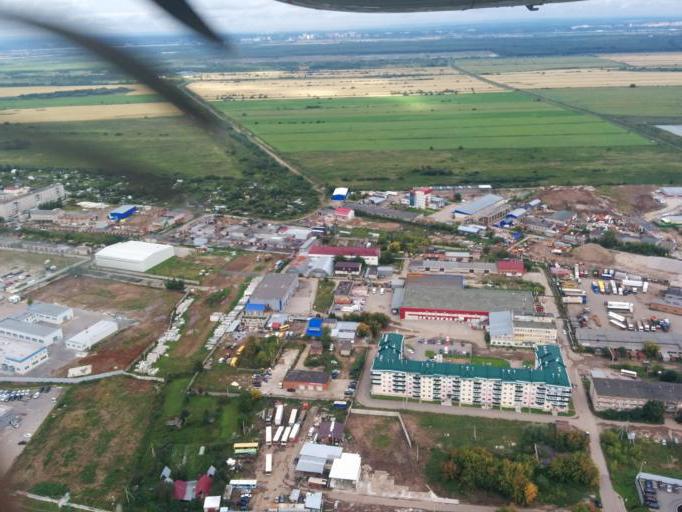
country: RU
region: Perm
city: Kondratovo
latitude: 57.9445
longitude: 56.0799
